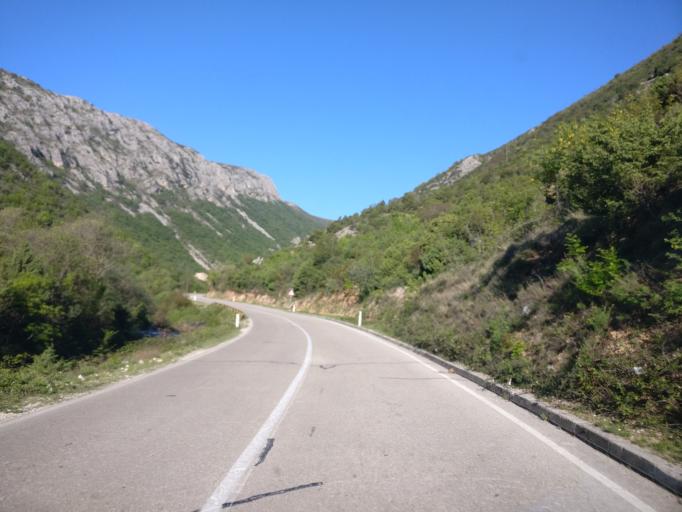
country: BA
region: Federation of Bosnia and Herzegovina
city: Stolac
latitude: 43.0723
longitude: 18.0444
